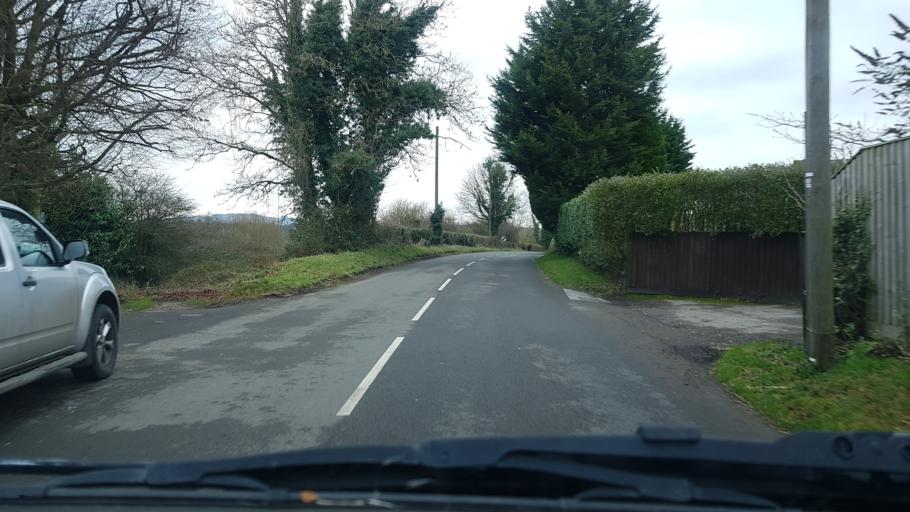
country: GB
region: England
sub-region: Wiltshire
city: Burbage
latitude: 51.3618
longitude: -1.6739
